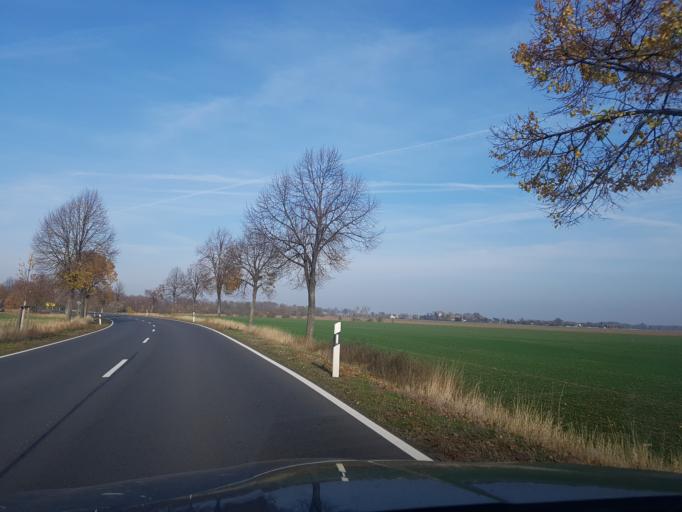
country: DE
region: Saxony
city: Torgau
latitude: 51.5598
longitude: 13.0242
